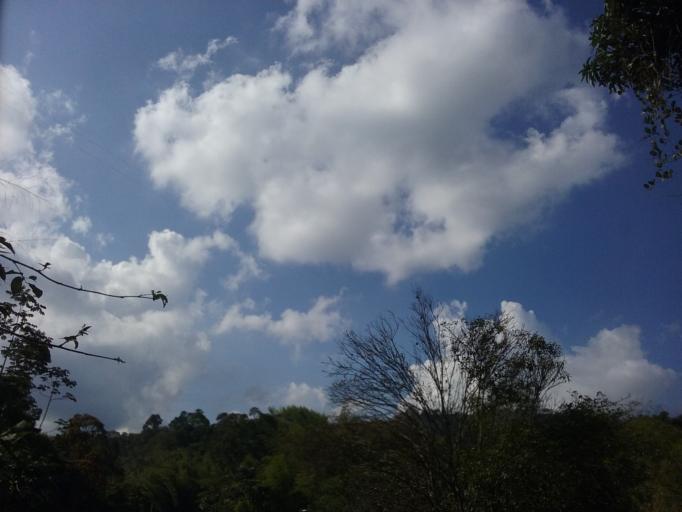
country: CO
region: Tolima
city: Libano
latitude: 4.8809
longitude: -75.0144
